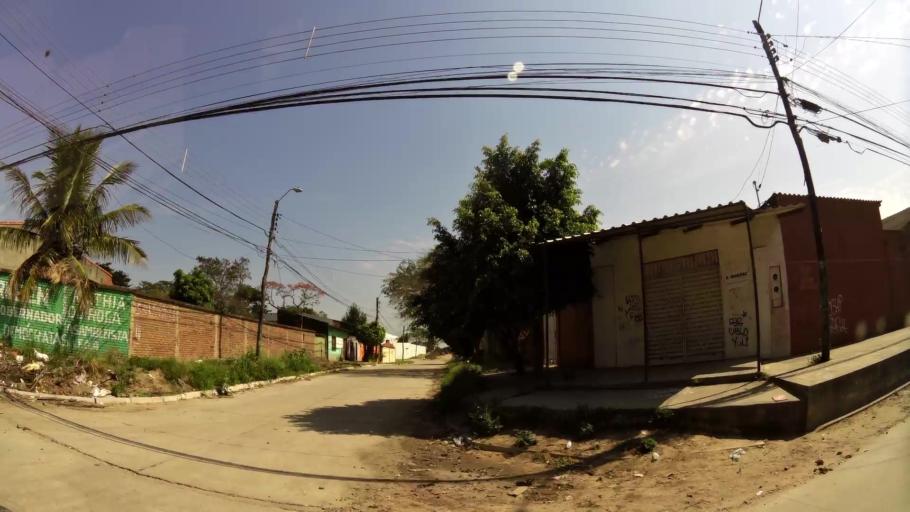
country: BO
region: Santa Cruz
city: Santa Cruz de la Sierra
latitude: -17.7469
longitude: -63.1806
